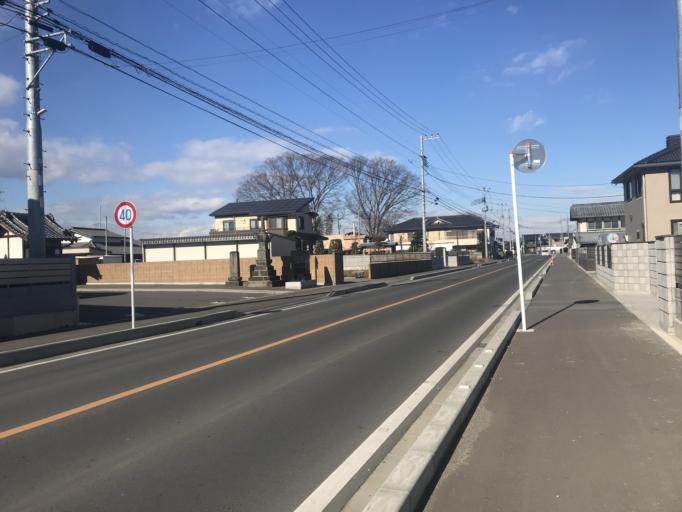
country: JP
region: Tochigi
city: Kaminokawa
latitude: 36.3736
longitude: 139.8788
